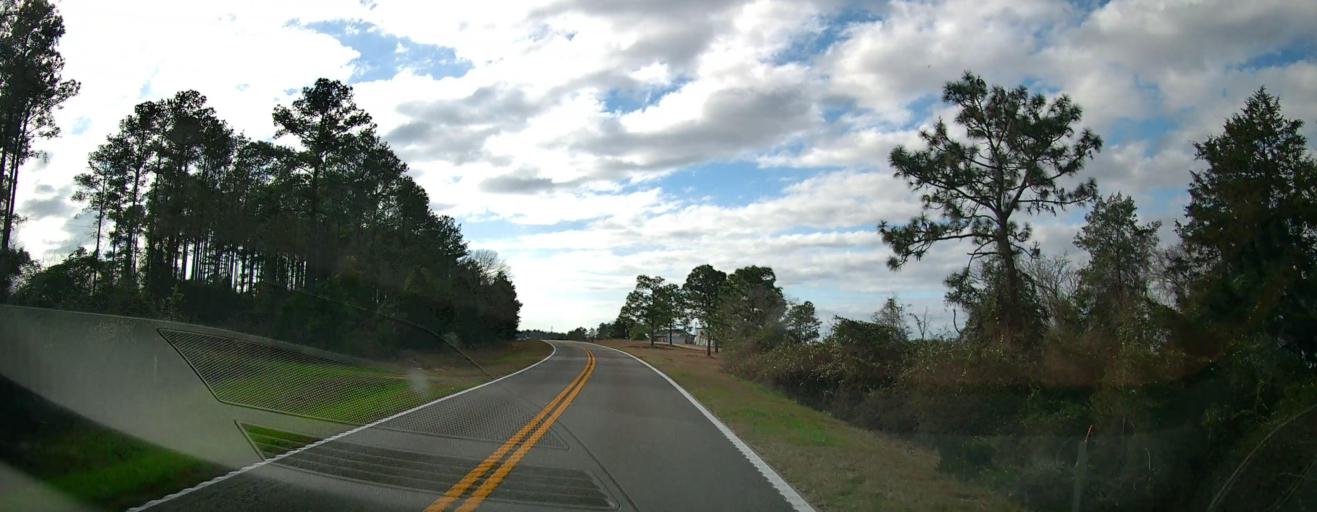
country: US
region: Georgia
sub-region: Marion County
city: Buena Vista
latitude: 32.4441
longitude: -84.5178
